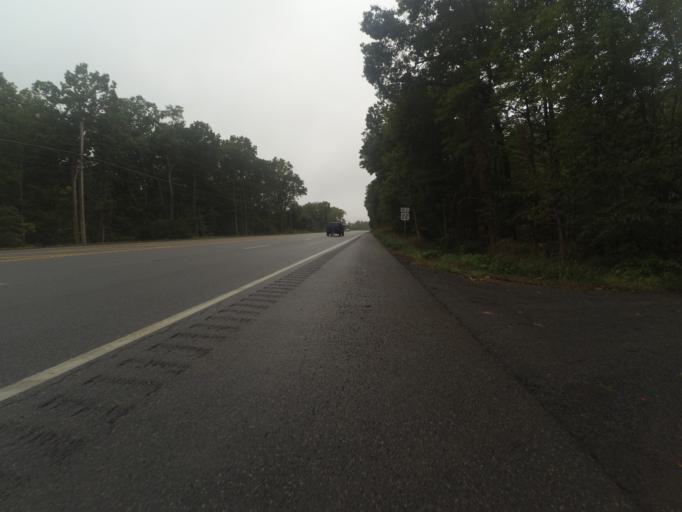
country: US
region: Pennsylvania
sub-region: Huntingdon County
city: Huntingdon
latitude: 40.4985
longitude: -78.0586
